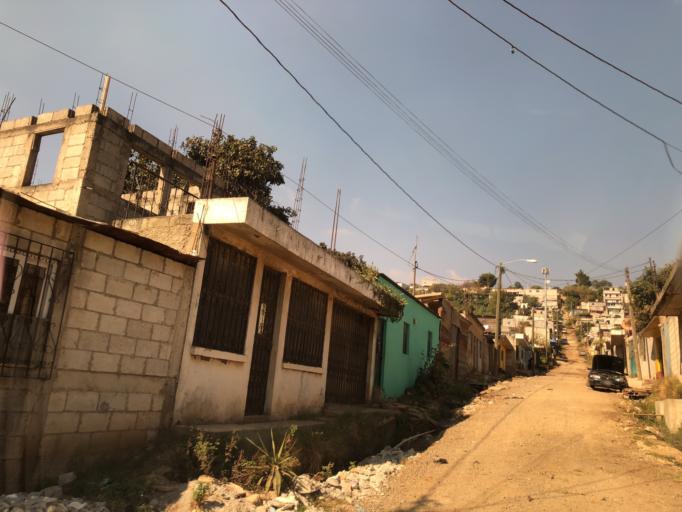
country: GT
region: Guatemala
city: Amatitlan
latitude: 14.4989
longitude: -90.5919
